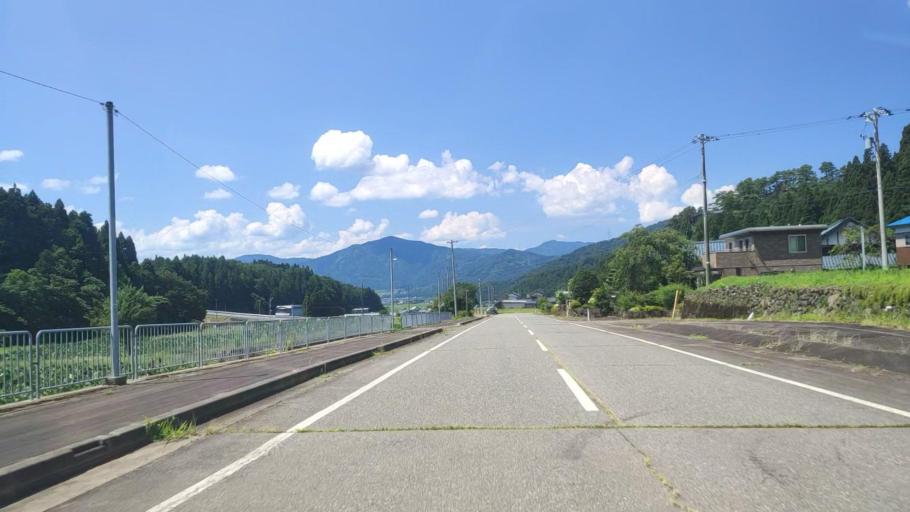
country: JP
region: Fukui
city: Katsuyama
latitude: 36.1035
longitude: 136.4935
